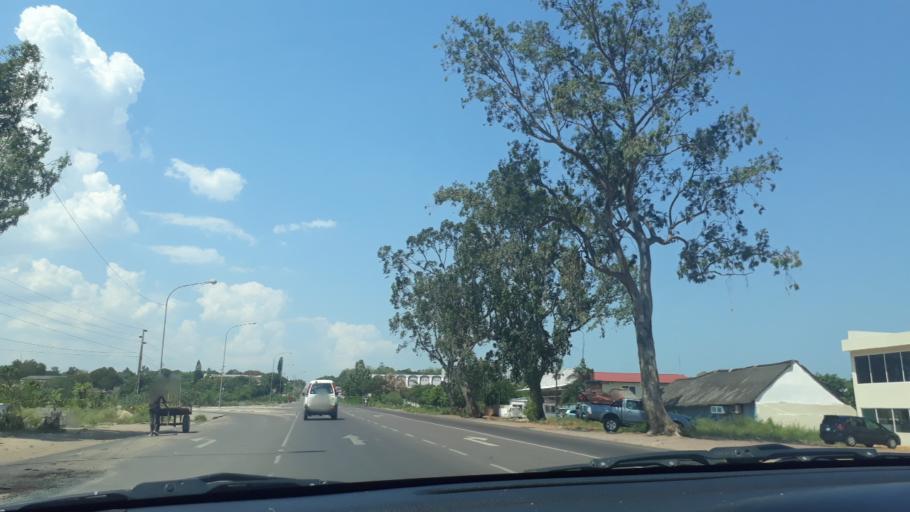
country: MZ
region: Maputo
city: Matola
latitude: -25.9680
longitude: 32.4434
